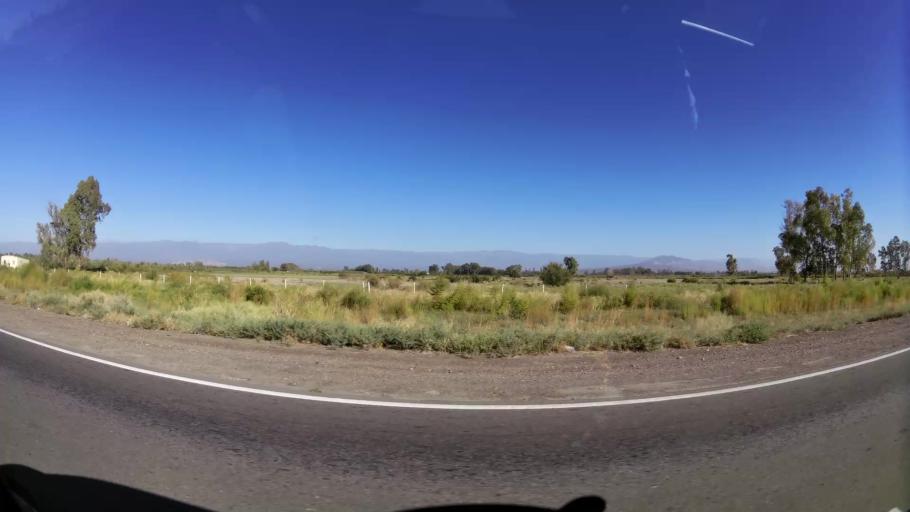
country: AR
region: Mendoza
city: General Lavalle
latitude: -32.7028
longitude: -68.6733
